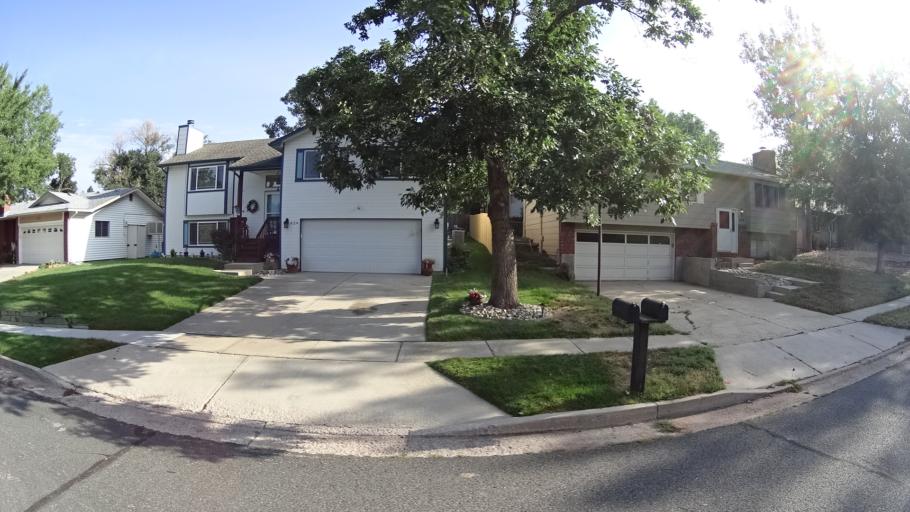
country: US
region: Colorado
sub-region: El Paso County
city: Colorado Springs
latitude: 38.8927
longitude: -104.8092
